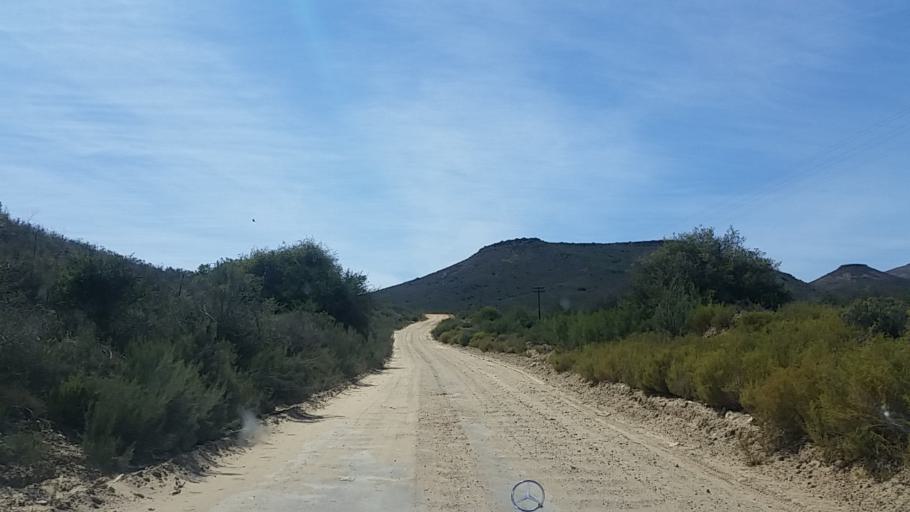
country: ZA
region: Western Cape
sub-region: Eden District Municipality
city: Knysna
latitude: -33.6391
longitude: 23.1477
